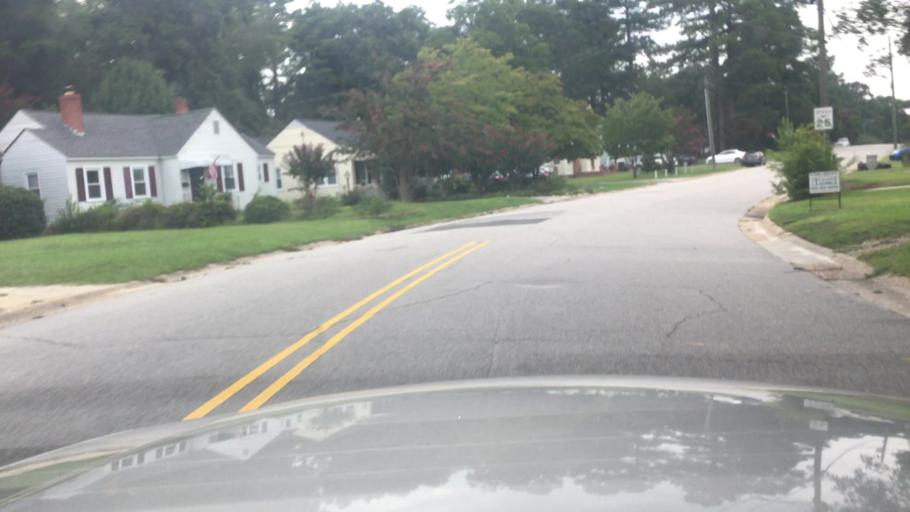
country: US
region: North Carolina
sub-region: Cumberland County
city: Fayetteville
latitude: 35.0713
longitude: -78.9162
